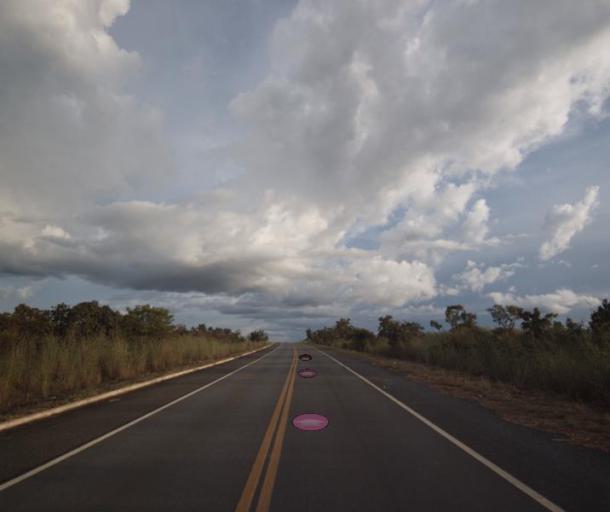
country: BR
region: Goias
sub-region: Barro Alto
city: Barro Alto
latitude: -14.8241
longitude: -48.6384
